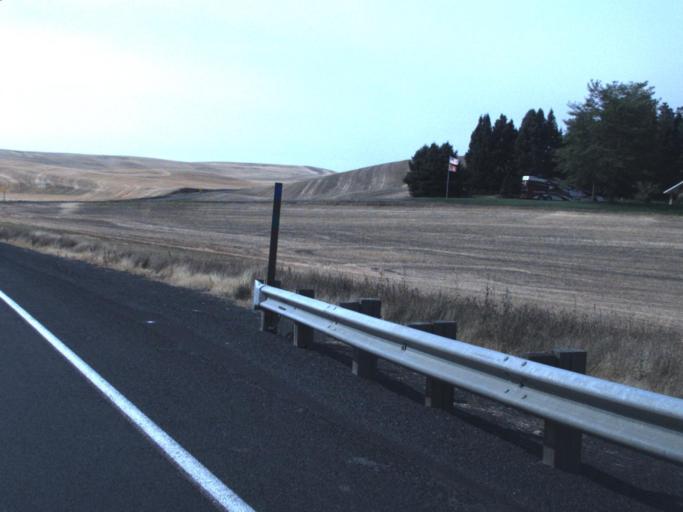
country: US
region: Washington
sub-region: Whitman County
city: Pullman
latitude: 46.7916
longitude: -117.1470
